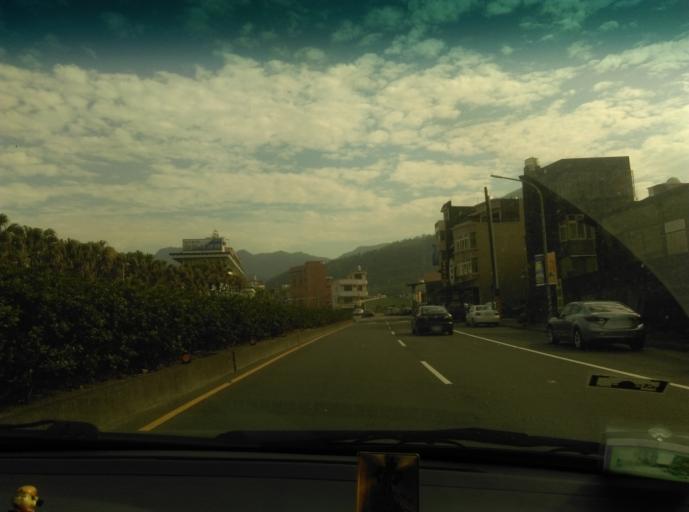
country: TW
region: Taiwan
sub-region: Keelung
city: Keelung
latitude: 25.1813
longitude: 121.6893
